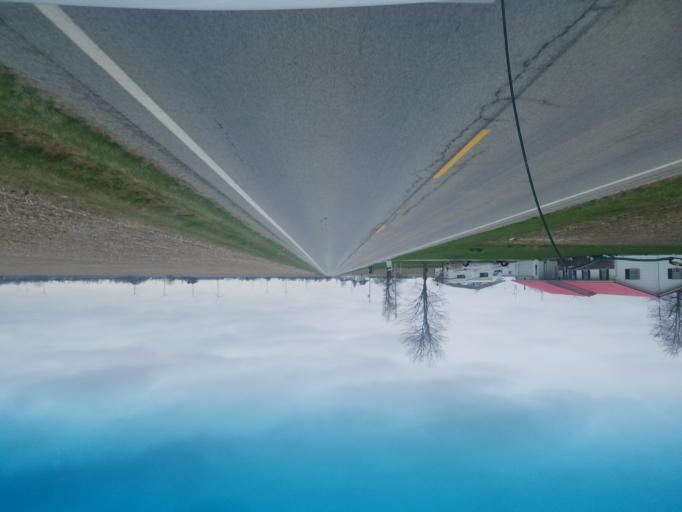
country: US
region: Ohio
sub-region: Van Wert County
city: Van Wert
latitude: 40.9320
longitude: -84.4865
